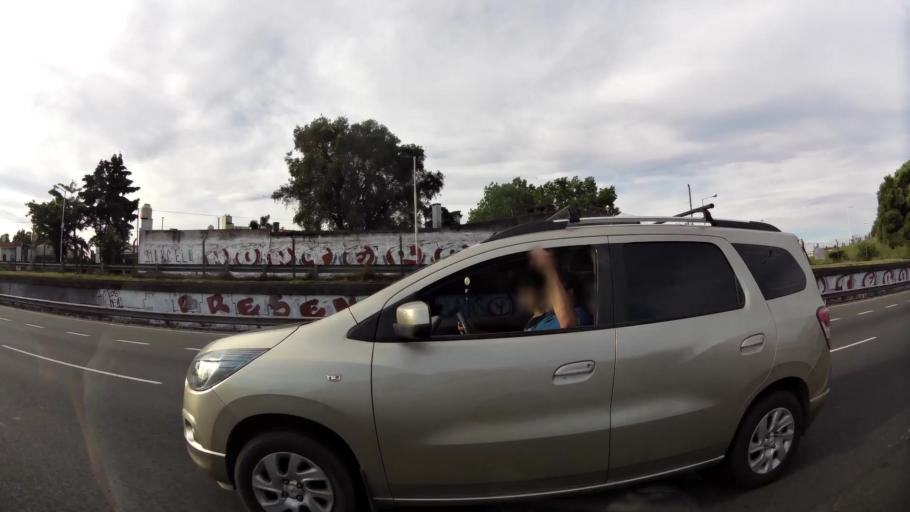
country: AR
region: Buenos Aires
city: Caseros
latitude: -34.6308
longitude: -58.5682
